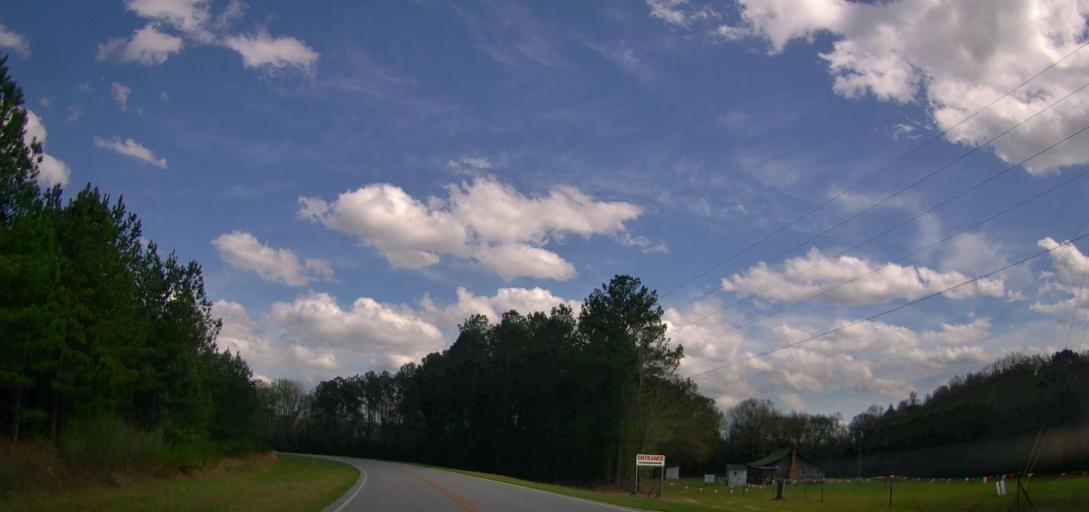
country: US
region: Georgia
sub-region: Wilkinson County
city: Gordon
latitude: 32.8263
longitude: -83.4235
